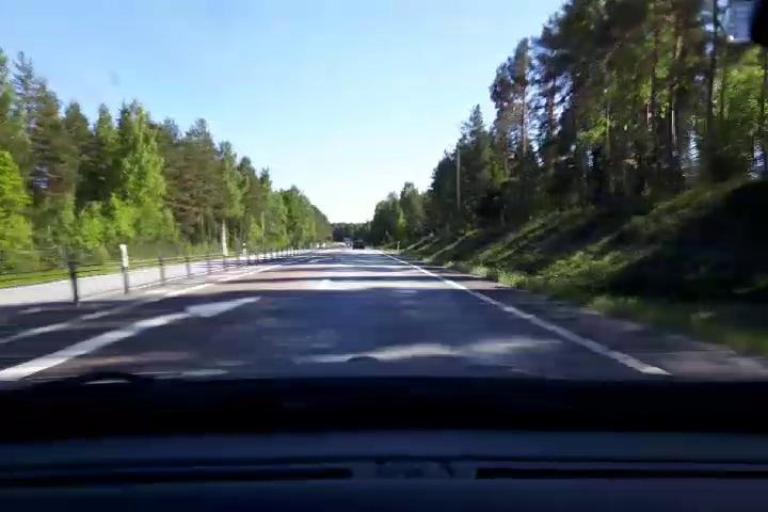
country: SE
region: Gaevleborg
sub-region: Gavle Kommun
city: Norrsundet
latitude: 61.0121
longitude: 16.9815
